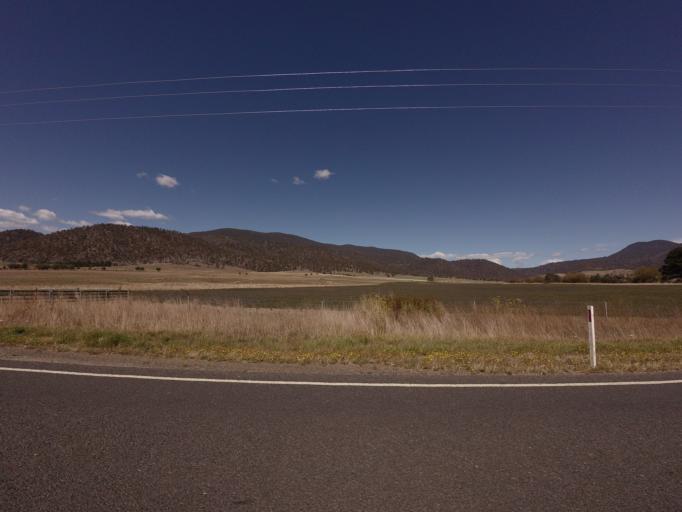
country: AU
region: Tasmania
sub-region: Break O'Day
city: St Helens
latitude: -41.7097
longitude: 147.8437
